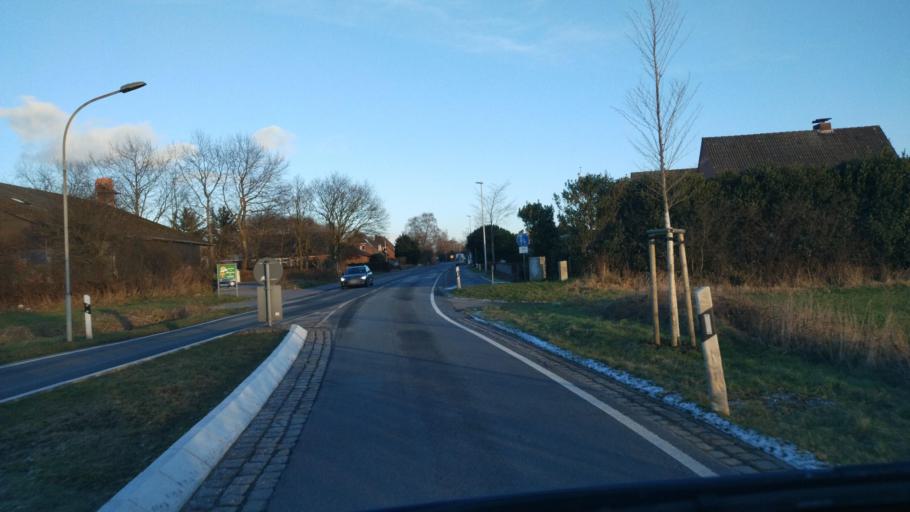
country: DE
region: Schleswig-Holstein
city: Ostenfeld
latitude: 54.4631
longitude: 9.2177
